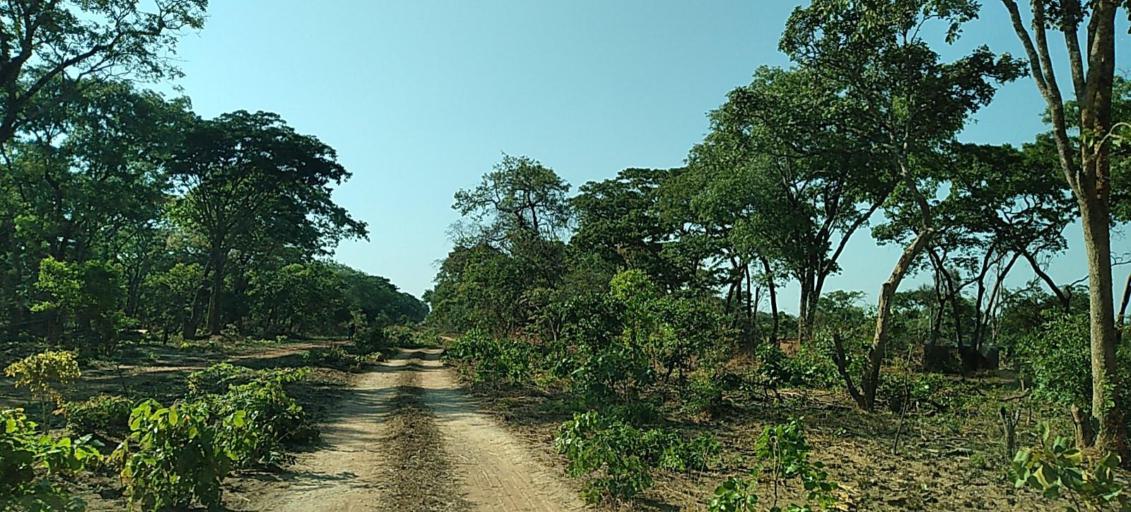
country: ZM
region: Central
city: Mkushi
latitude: -13.4567
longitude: 28.9096
